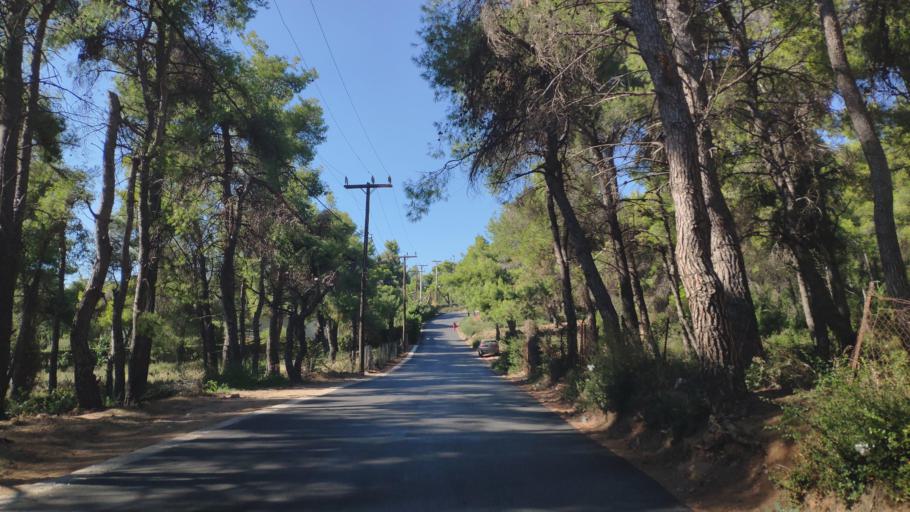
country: GR
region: Attica
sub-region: Nomarchia Anatolikis Attikis
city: Drosia
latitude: 38.1250
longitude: 23.8723
